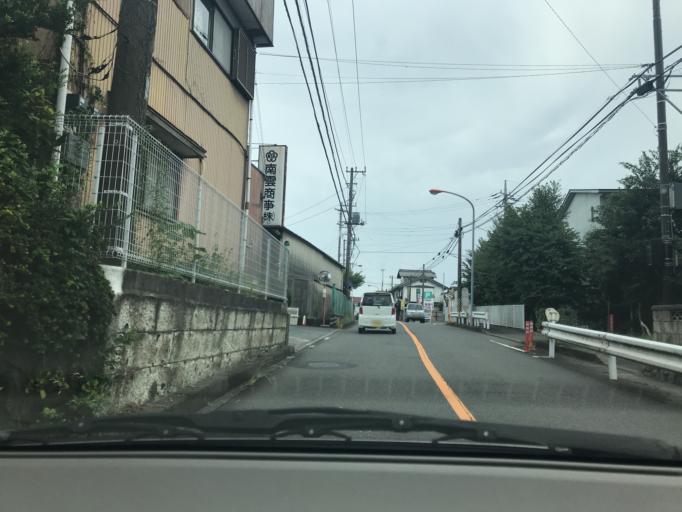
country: JP
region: Kanagawa
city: Fujisawa
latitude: 35.3842
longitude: 139.4387
